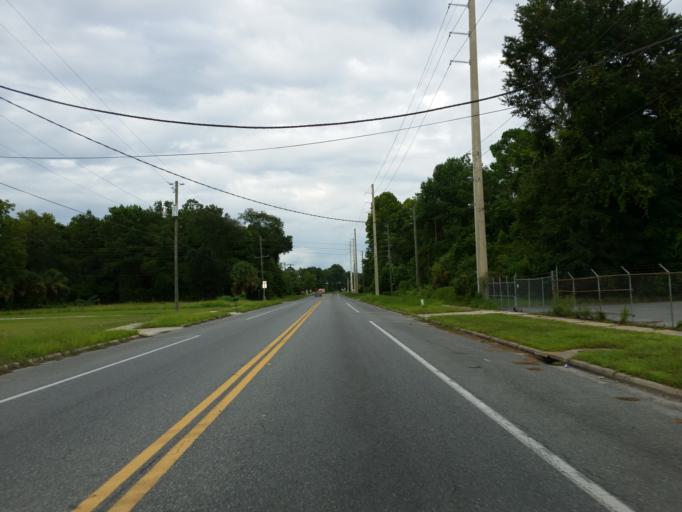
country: US
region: Florida
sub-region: Columbia County
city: Five Points
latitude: 30.2032
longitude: -82.6422
